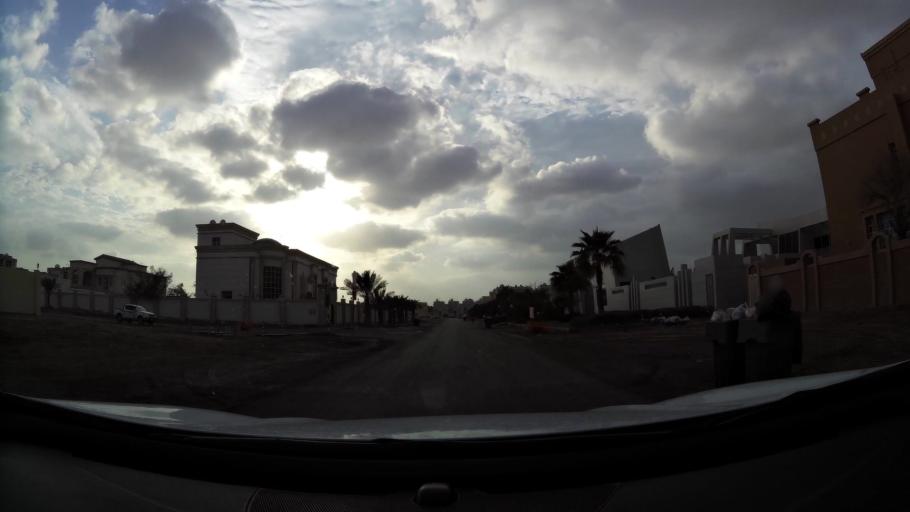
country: AE
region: Abu Dhabi
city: Abu Dhabi
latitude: 24.3521
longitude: 54.5573
